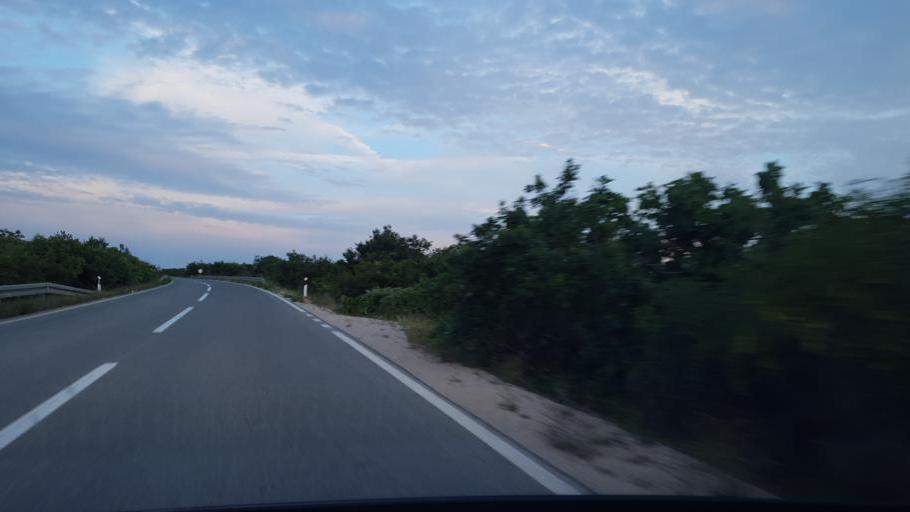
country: HR
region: Primorsko-Goranska
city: Punat
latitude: 45.0368
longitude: 14.6484
